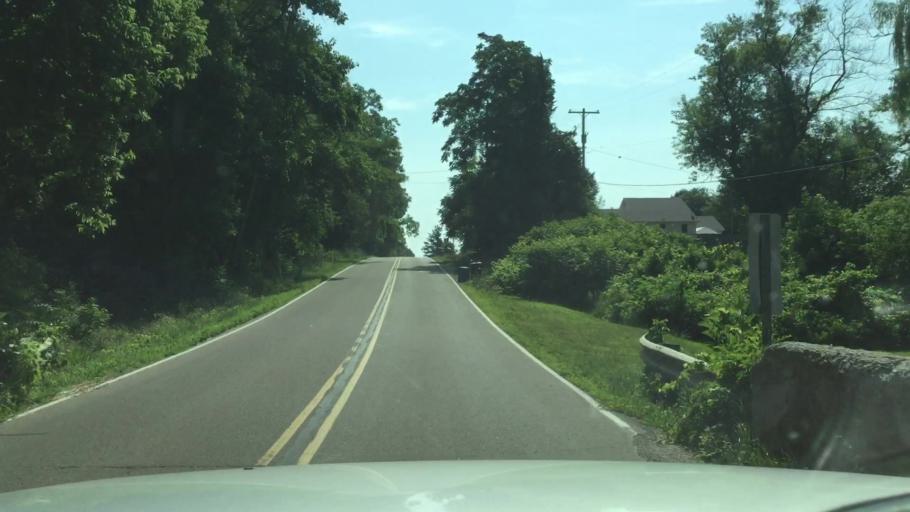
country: US
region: Michigan
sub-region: Genesee County
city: Flushing
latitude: 43.1334
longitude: -83.8328
